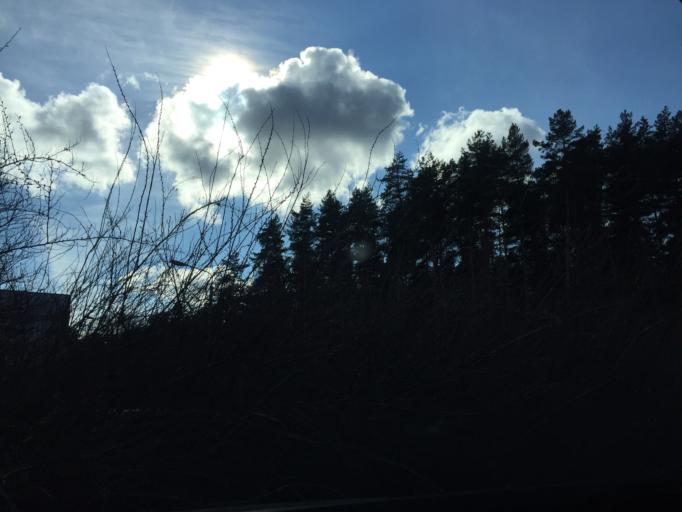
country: LV
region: Kekava
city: Kekava
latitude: 56.8299
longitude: 24.1985
